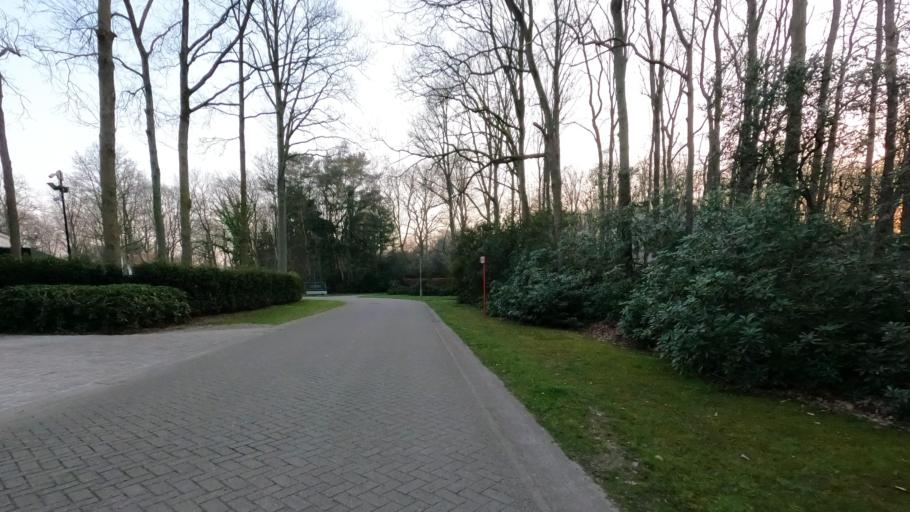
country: BE
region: Flanders
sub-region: Provincie Antwerpen
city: Schilde
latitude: 51.2438
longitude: 4.5659
